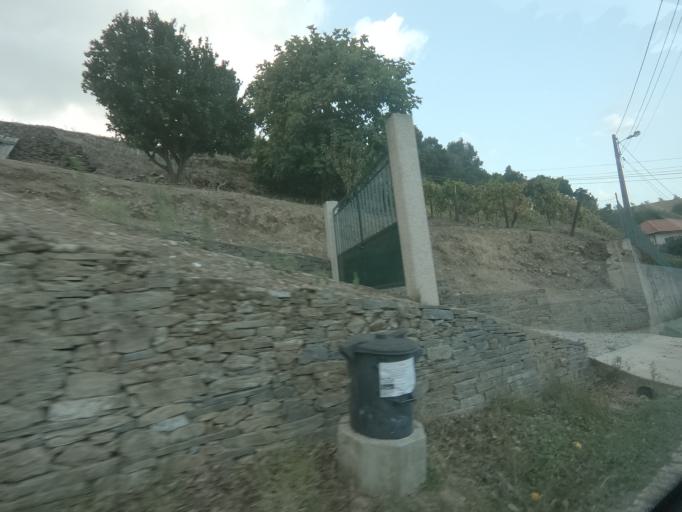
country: PT
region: Vila Real
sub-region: Mesao Frio
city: Mesao Frio
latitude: 41.1814
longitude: -7.8563
